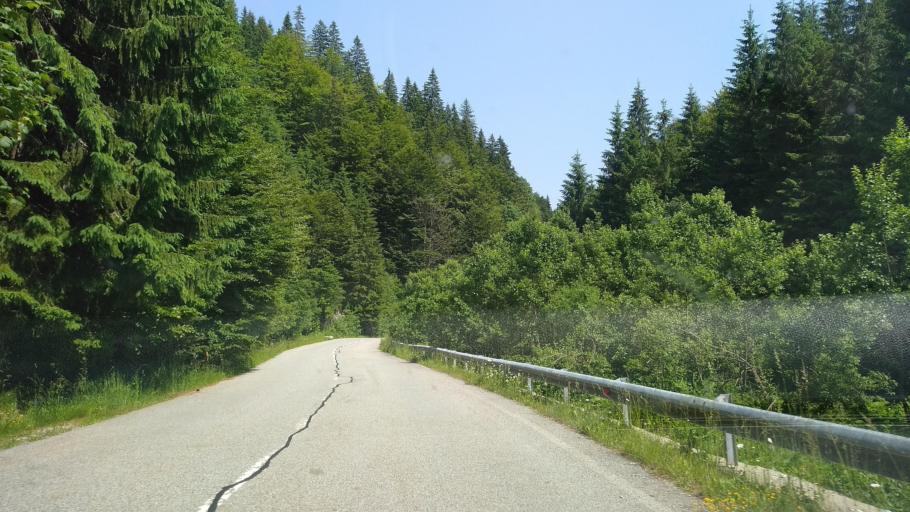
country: RO
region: Gorj
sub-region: Comuna Runcu
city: Valea Mare
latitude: 45.2776
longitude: 22.9351
